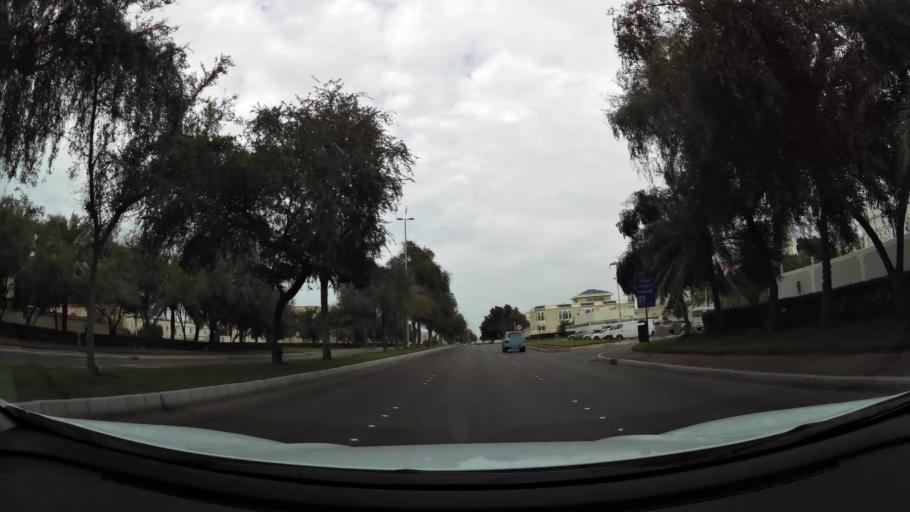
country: AE
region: Abu Dhabi
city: Abu Dhabi
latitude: 24.4290
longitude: 54.4012
